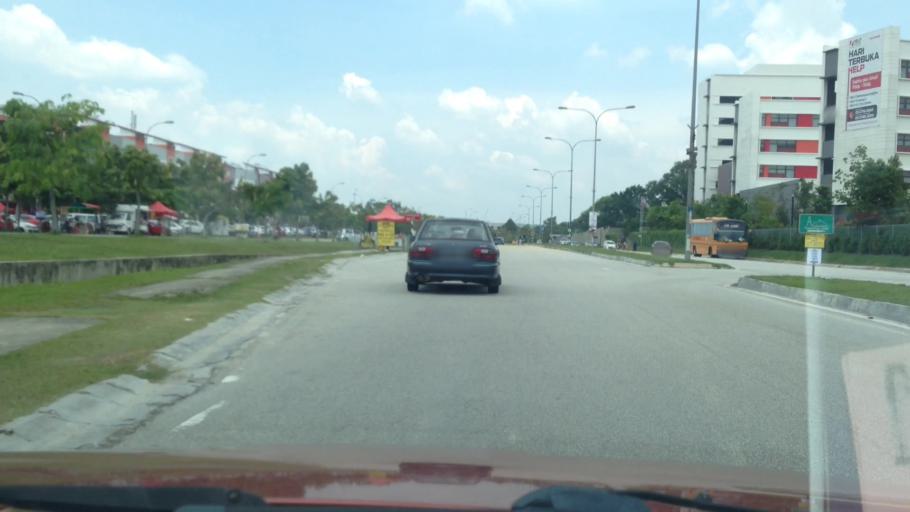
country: MY
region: Selangor
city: Kampung Baru Subang
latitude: 3.1766
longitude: 101.5489
